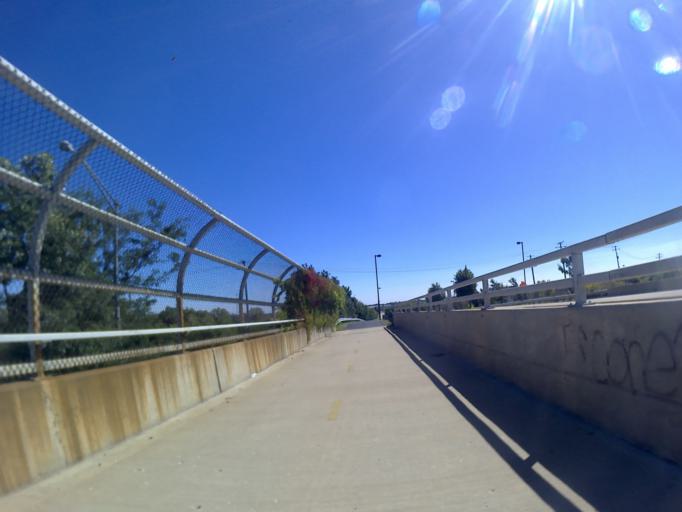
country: US
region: Illinois
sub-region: Cook County
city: Lemont
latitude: 41.7076
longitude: -88.0242
